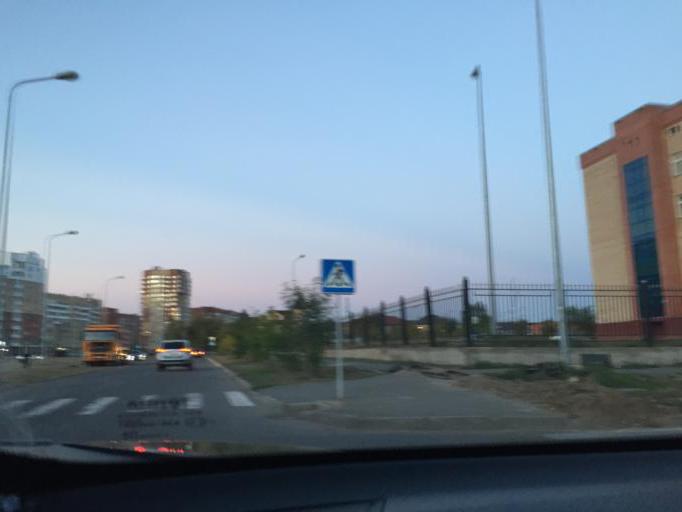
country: KZ
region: Astana Qalasy
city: Astana
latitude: 51.1447
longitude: 71.4776
